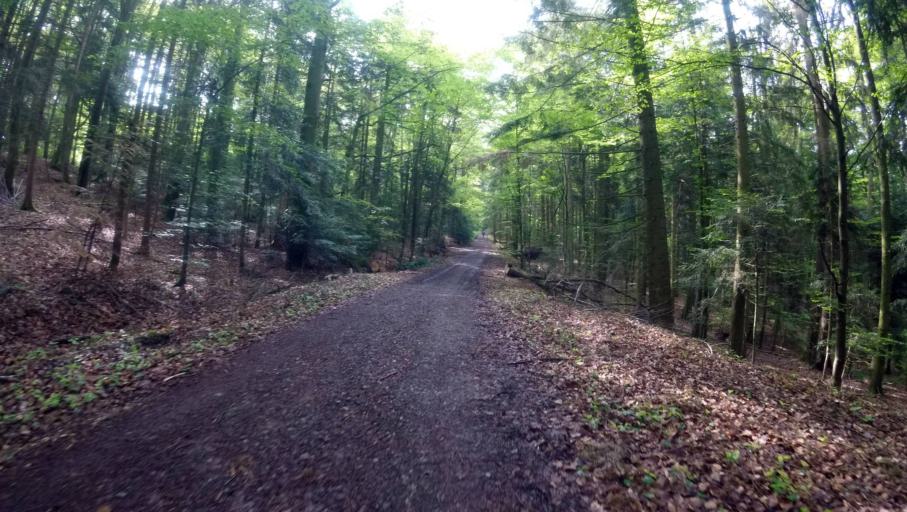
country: DE
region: Baden-Wuerttemberg
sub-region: Regierungsbezirk Stuttgart
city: Kaisersbach
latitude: 48.9184
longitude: 9.6145
